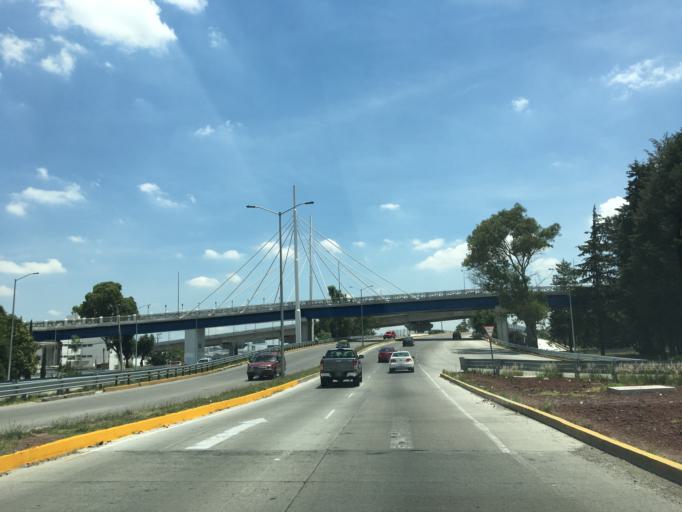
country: MX
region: Puebla
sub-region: Cuautlancingo
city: Sanctorum
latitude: 19.0955
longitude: -98.2300
